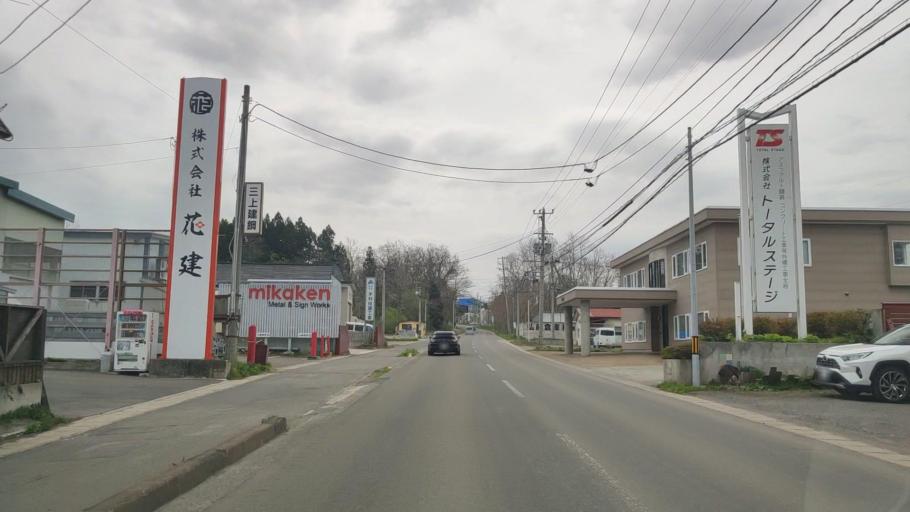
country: JP
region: Aomori
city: Aomori Shi
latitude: 40.7776
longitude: 140.7943
